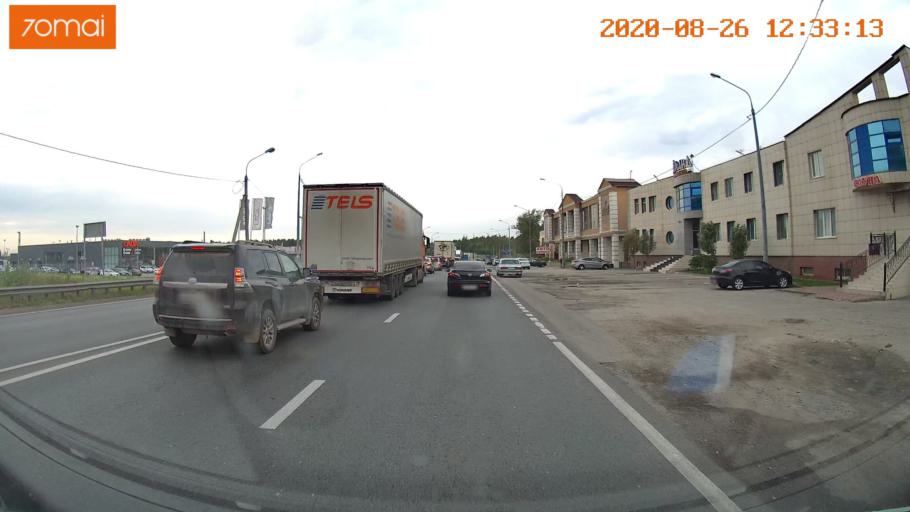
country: RU
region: Rjazan
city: Ryazan'
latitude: 54.5811
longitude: 39.7788
